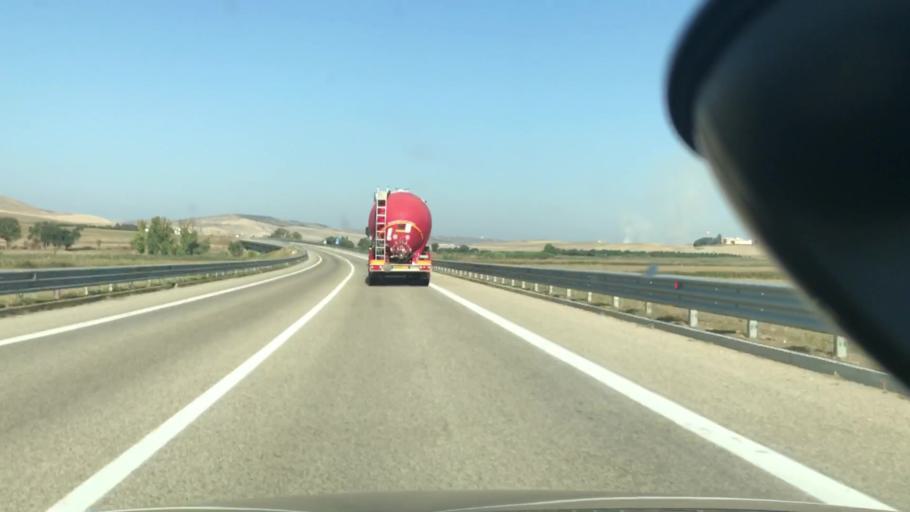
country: IT
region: Basilicate
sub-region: Provincia di Matera
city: Irsina
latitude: 40.7810
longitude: 16.3137
